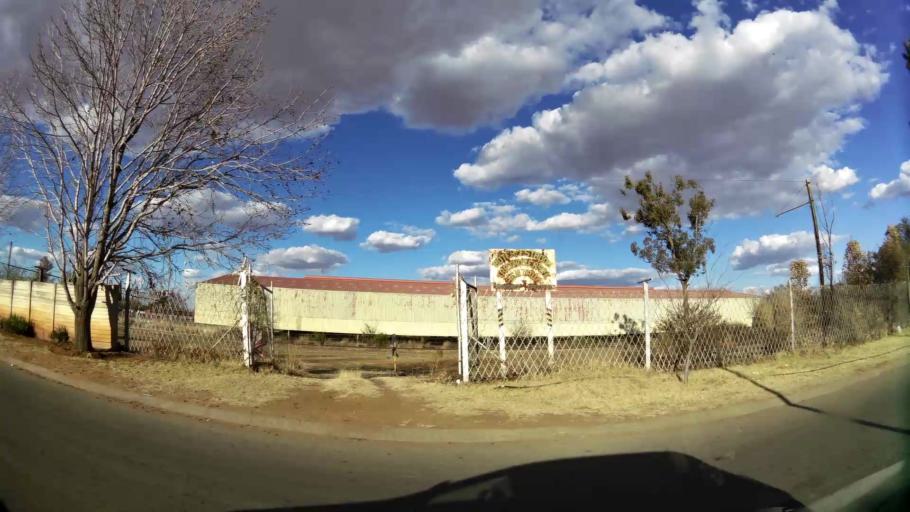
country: ZA
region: North-West
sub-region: Dr Kenneth Kaunda District Municipality
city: Potchefstroom
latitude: -26.7115
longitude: 27.0814
